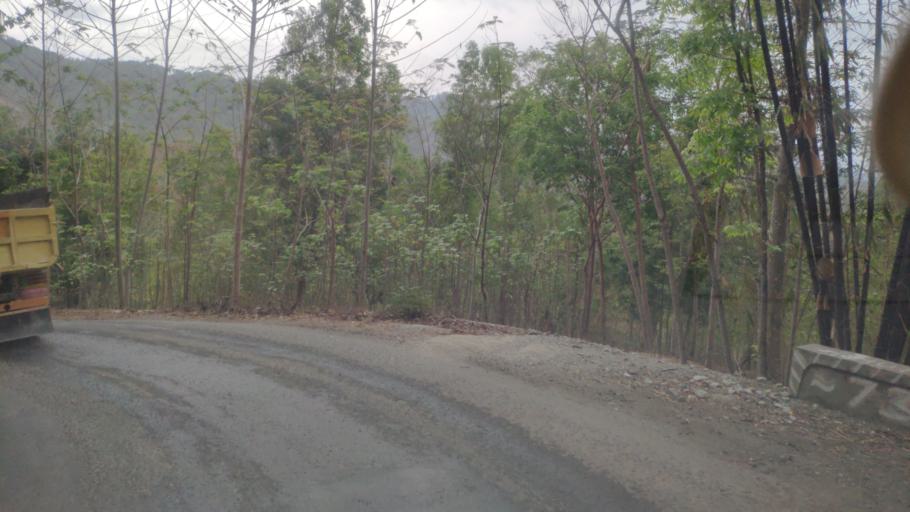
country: ID
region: Central Java
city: Gombong
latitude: -7.4961
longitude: 109.5460
